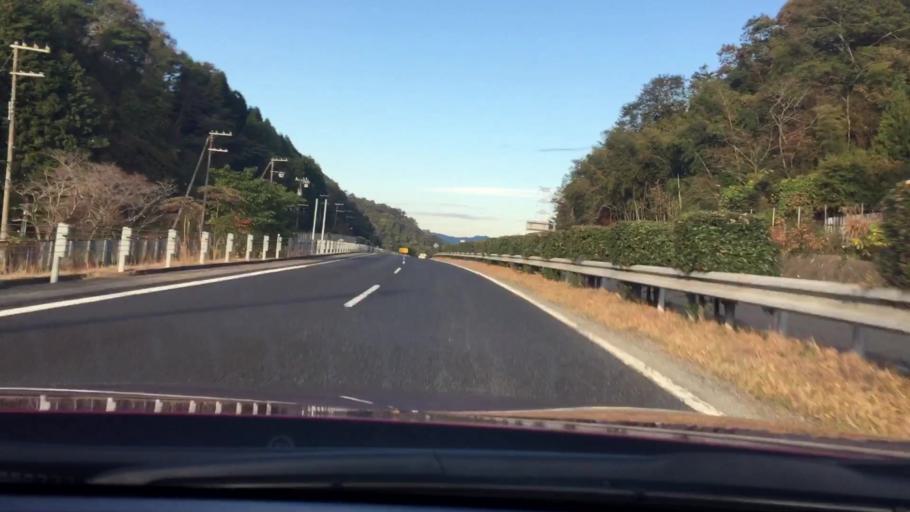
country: JP
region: Hyogo
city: Yamazakicho-nakabirose
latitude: 34.9803
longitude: 134.6217
